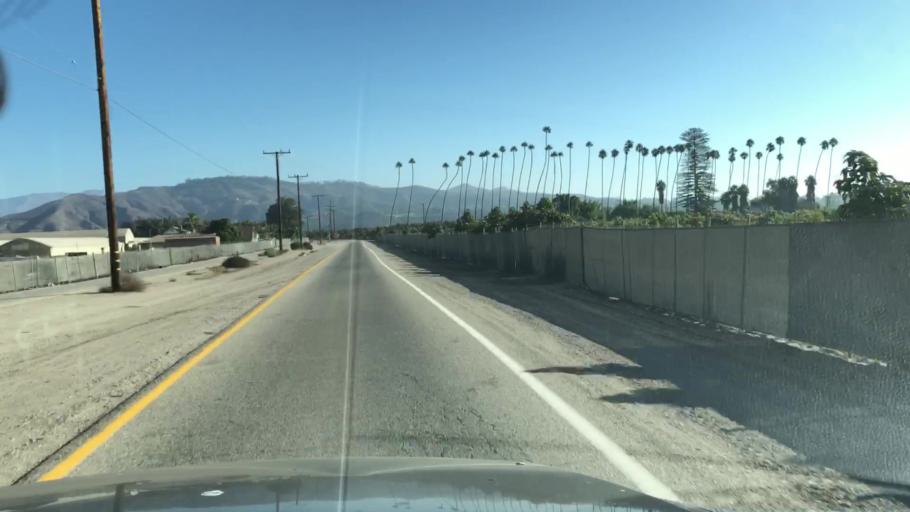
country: US
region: California
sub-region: Ventura County
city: Saticoy
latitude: 34.2614
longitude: -119.1307
